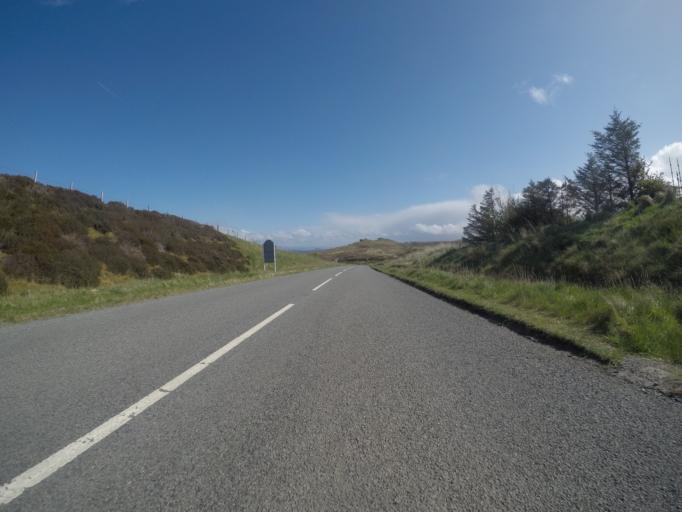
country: GB
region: Scotland
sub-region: Highland
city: Portree
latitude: 57.6118
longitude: -6.1770
